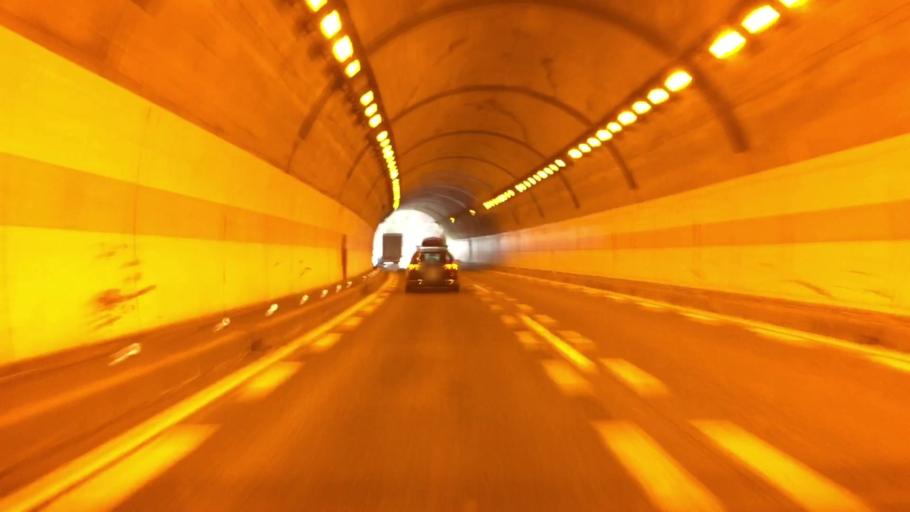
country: JP
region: Gunma
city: Numata
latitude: 36.7552
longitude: 138.9671
